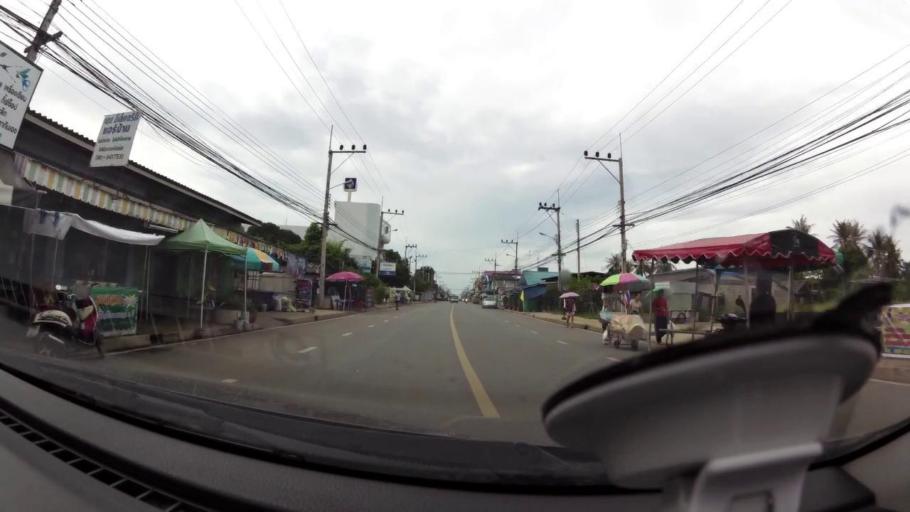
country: TH
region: Prachuap Khiri Khan
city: Pran Buri
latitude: 12.3981
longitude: 99.9901
